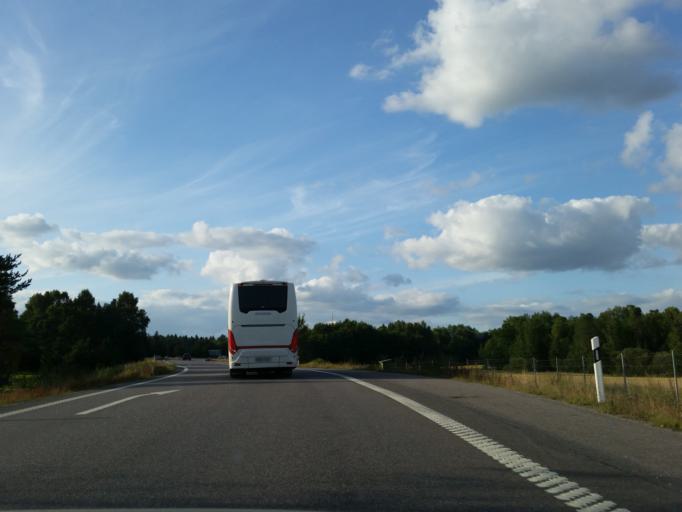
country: SE
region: Stockholm
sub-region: Sodertalje Kommun
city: Pershagen
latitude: 59.0880
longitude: 17.6016
